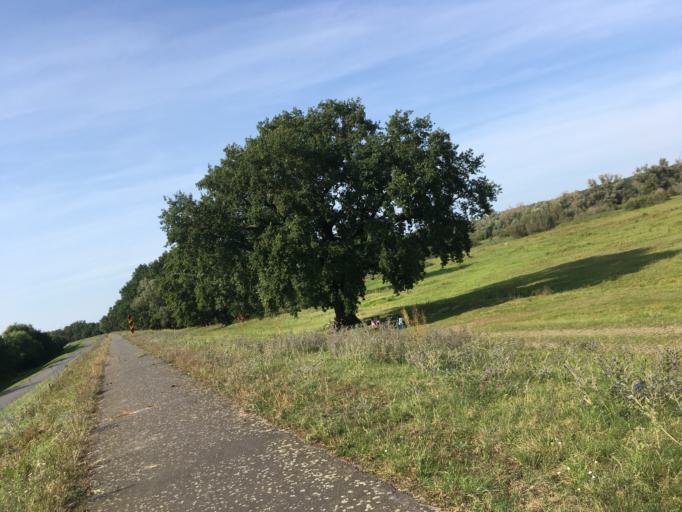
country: DE
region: Brandenburg
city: Vogelsang
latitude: 52.2481
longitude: 14.6931
